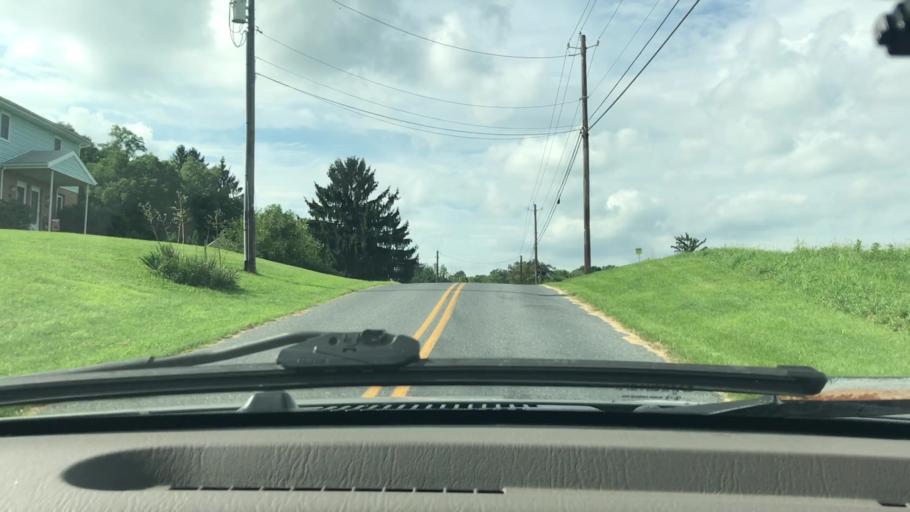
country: US
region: Pennsylvania
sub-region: Lancaster County
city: Elizabethtown
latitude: 40.1739
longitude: -76.6211
